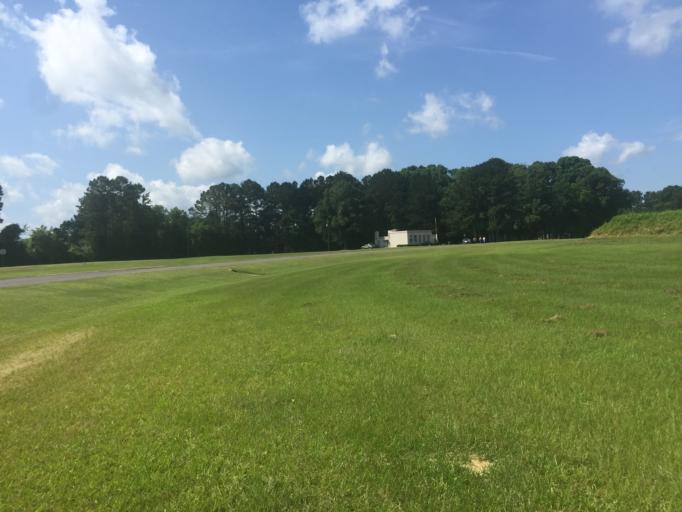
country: US
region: Alabama
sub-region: Hale County
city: Moundville
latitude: 33.0044
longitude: -87.6275
